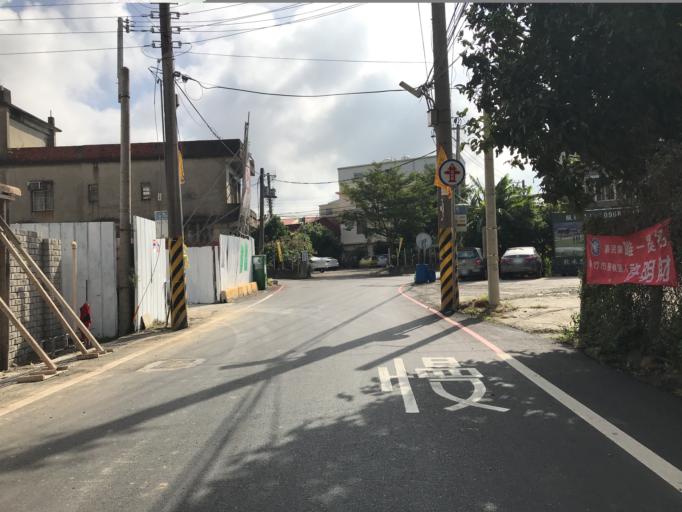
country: TW
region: Taiwan
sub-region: Hsinchu
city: Zhubei
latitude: 24.8102
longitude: 121.0034
